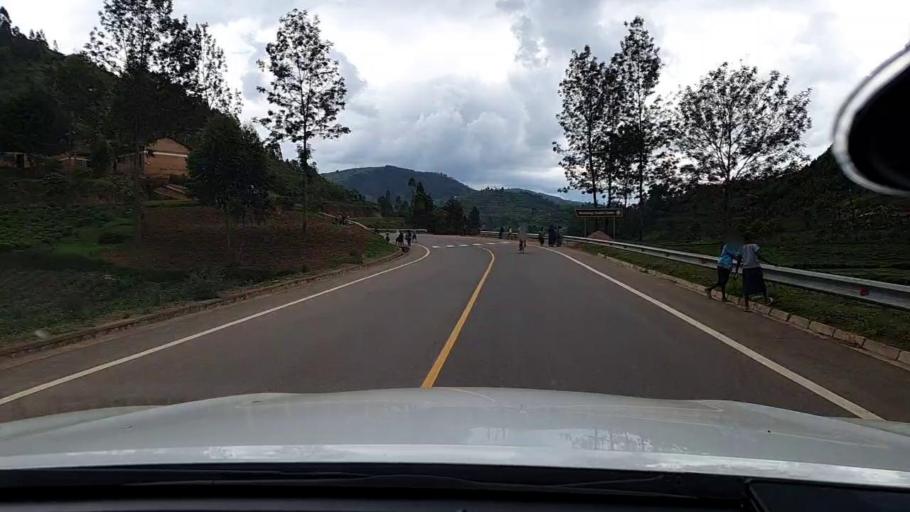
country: RW
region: Northern Province
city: Byumba
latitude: -1.6540
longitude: 29.9121
